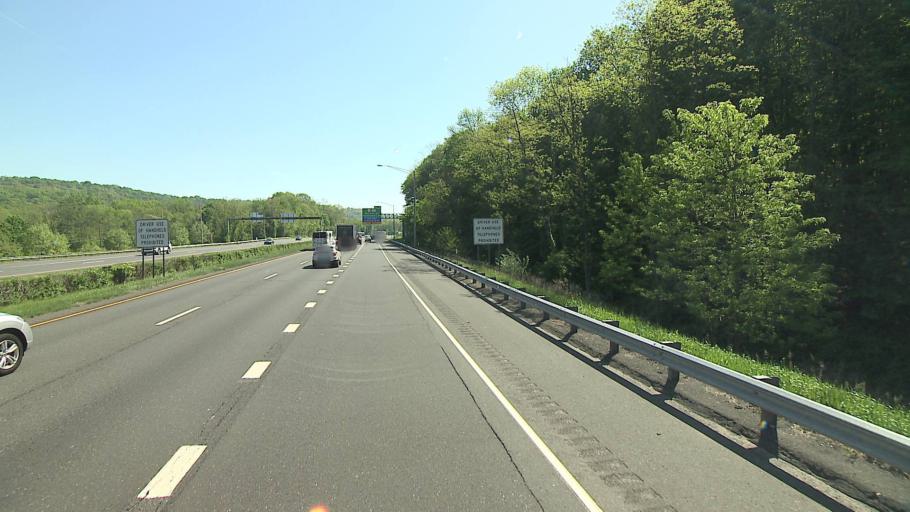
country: US
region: New York
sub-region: Putnam County
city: Peach Lake
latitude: 41.3909
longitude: -73.5365
